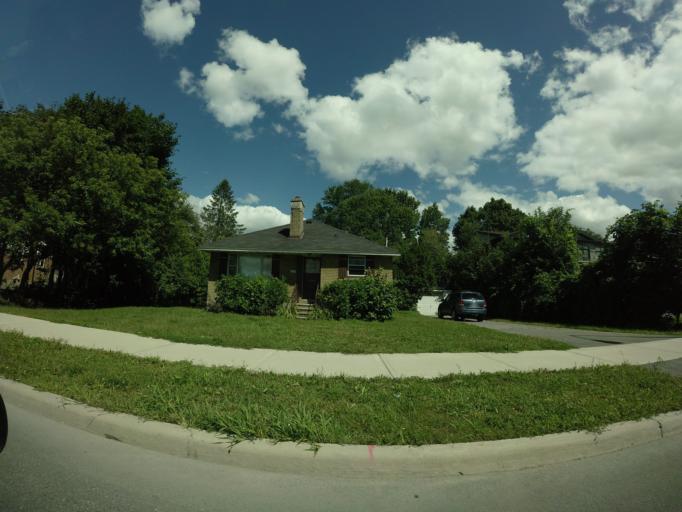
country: CA
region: Ontario
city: Bells Corners
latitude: 45.3566
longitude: -75.7656
